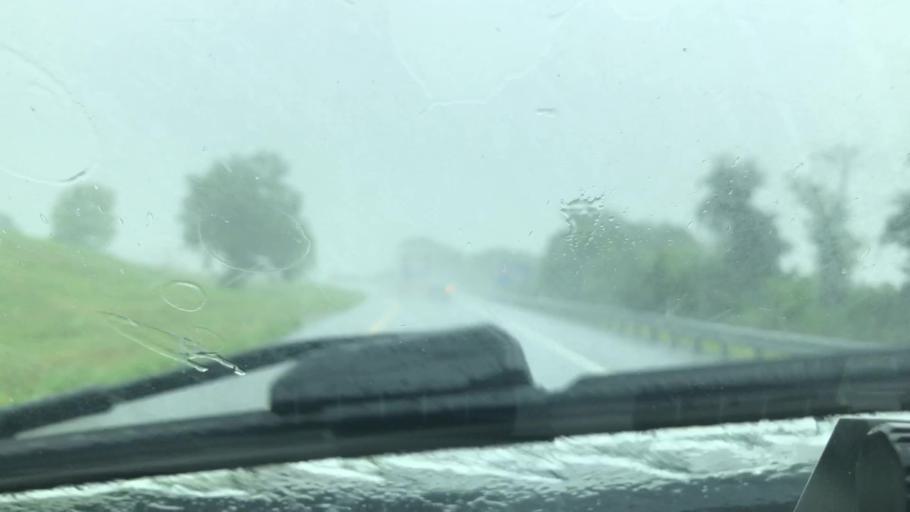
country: US
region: Pennsylvania
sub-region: Dauphin County
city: Skyline View
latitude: 40.3513
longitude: -76.7214
